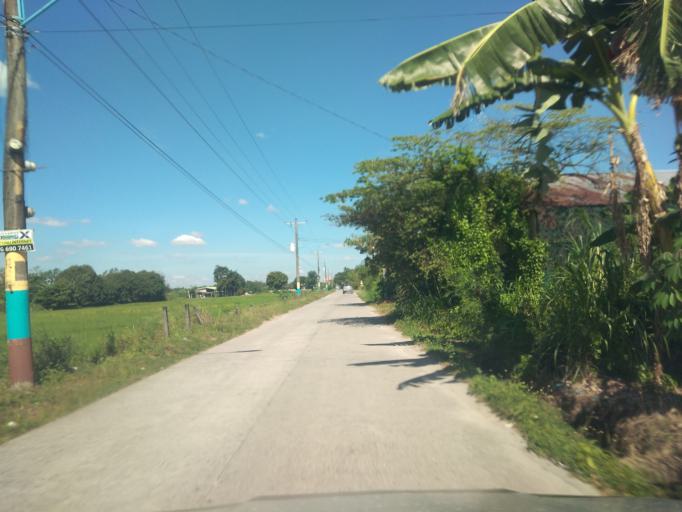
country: PH
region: Central Luzon
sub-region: Province of Pampanga
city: Bacolor
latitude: 15.0193
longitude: 120.6400
